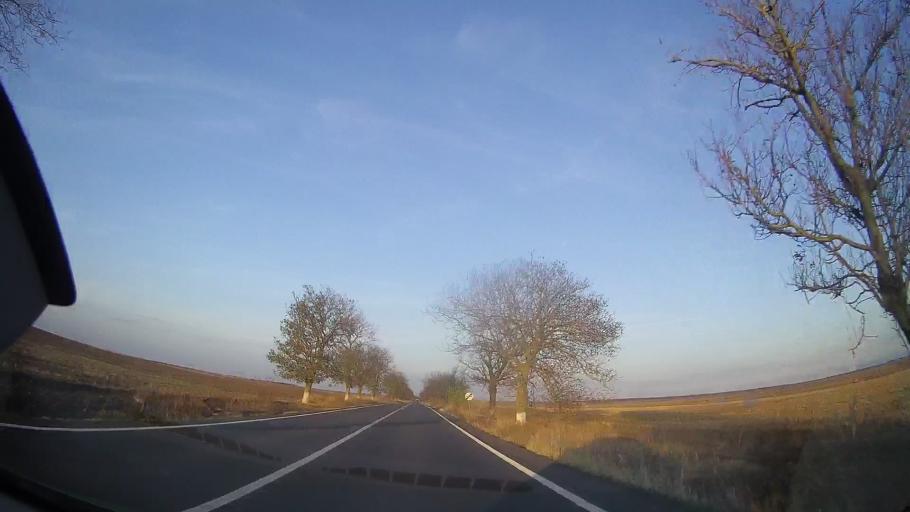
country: RO
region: Constanta
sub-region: Comuna Amzacea
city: Amzacea
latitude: 43.9387
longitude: 28.3687
